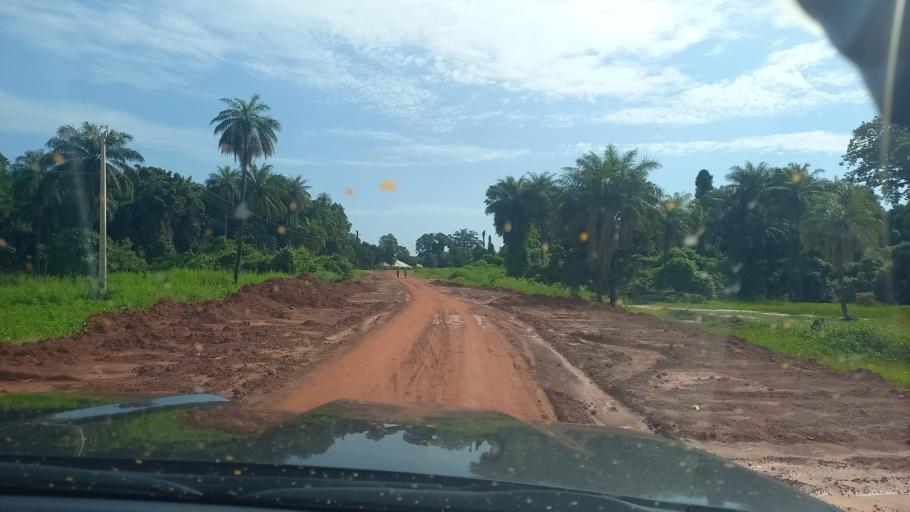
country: SN
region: Ziguinchor
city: Ziguinchor
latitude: 12.6745
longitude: -16.2003
